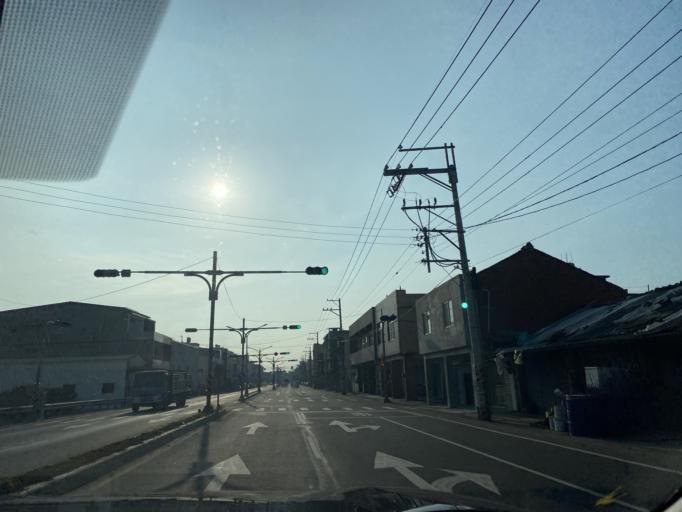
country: TW
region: Taiwan
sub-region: Changhua
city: Chang-hua
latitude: 23.9552
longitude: 120.4457
